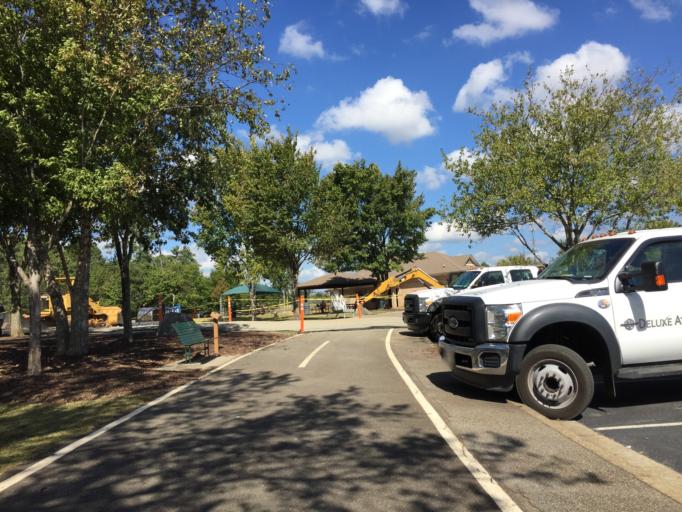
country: US
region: Georgia
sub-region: Fulton County
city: Alpharetta
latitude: 34.0185
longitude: -84.2668
